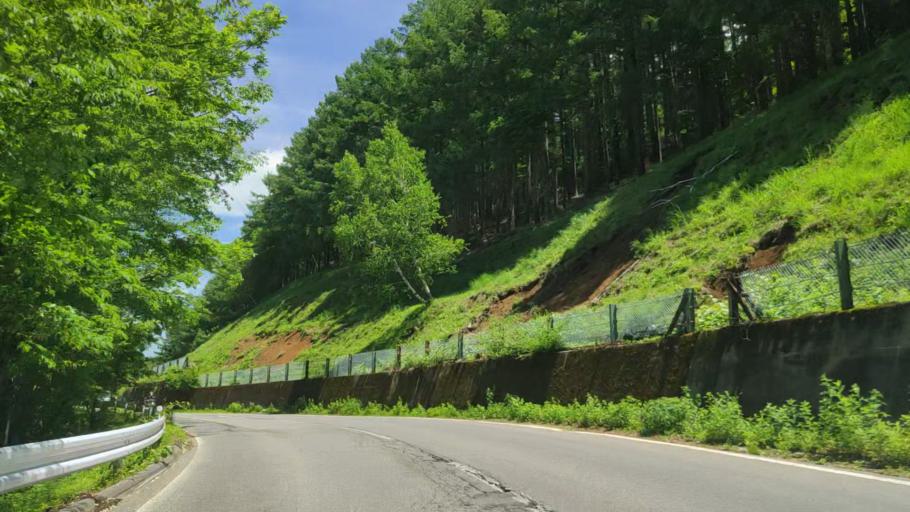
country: JP
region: Nagano
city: Suwa
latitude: 36.1502
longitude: 138.2380
